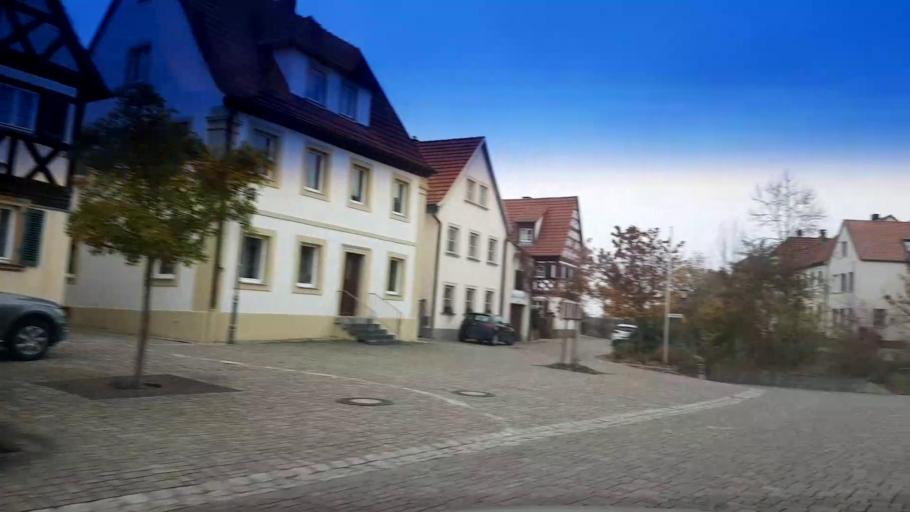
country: DE
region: Bavaria
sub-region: Upper Franconia
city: Rattelsdorf
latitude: 50.0155
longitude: 10.8868
